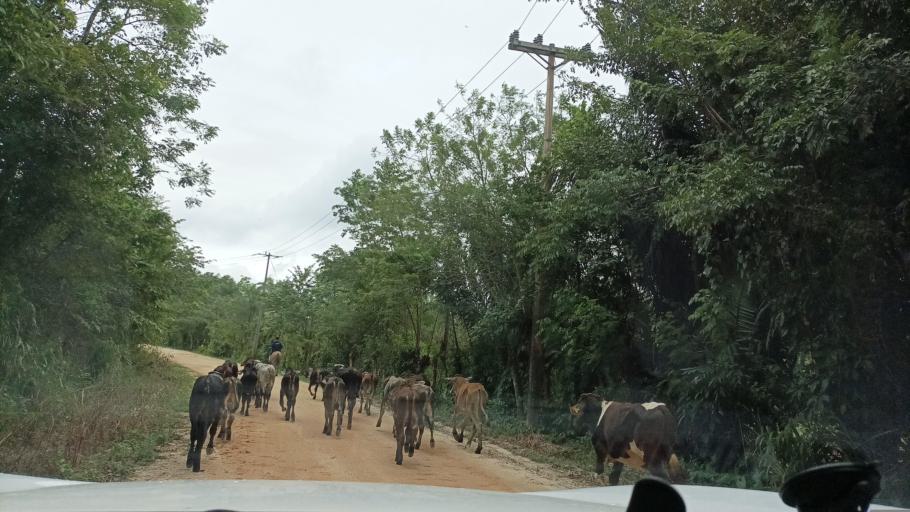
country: MX
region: Veracruz
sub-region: Moloacan
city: Cuichapa
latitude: 17.8193
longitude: -94.3538
